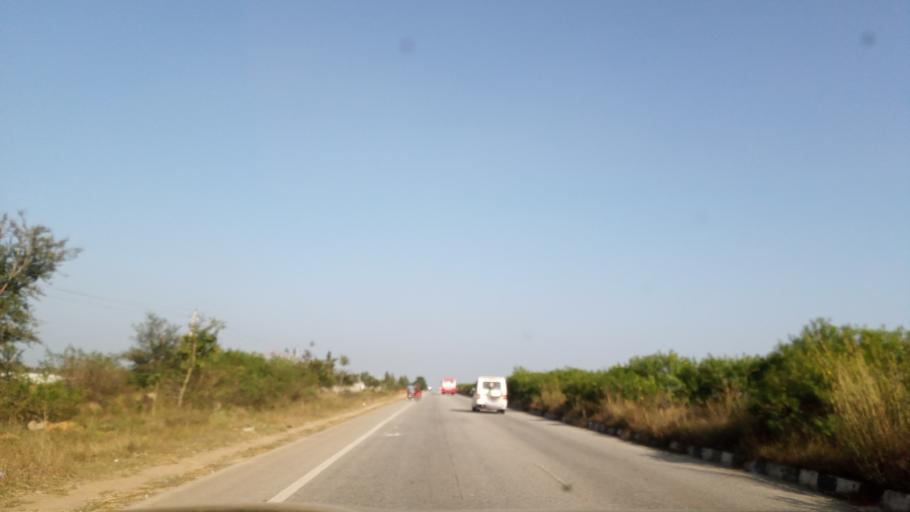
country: IN
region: Karnataka
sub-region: Kolar
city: Mulbagal
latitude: 13.1549
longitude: 78.3366
